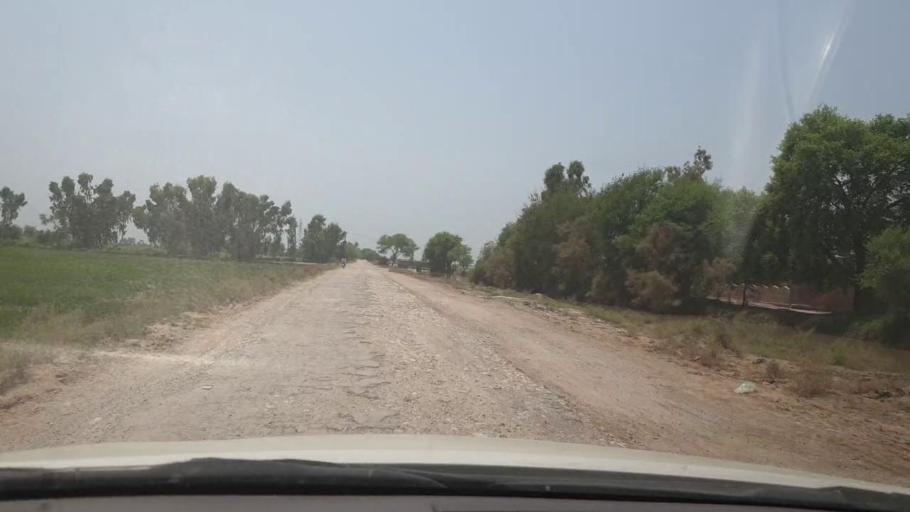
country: PK
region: Sindh
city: Shikarpur
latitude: 28.0976
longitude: 68.5795
